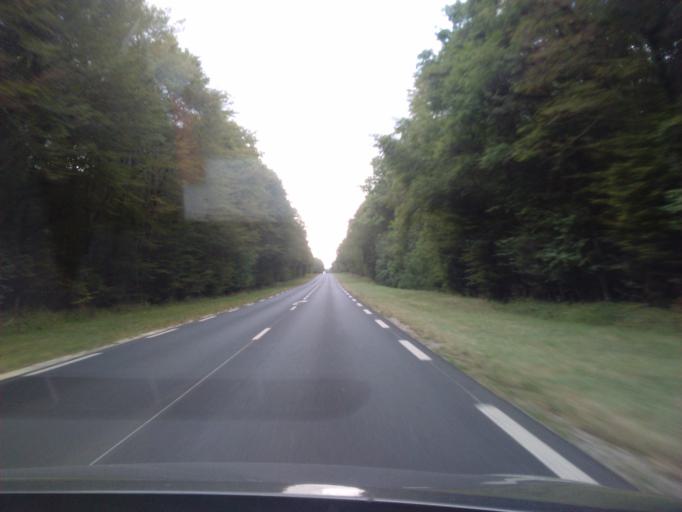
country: FR
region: Centre
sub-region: Departement du Loir-et-Cher
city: Cellettes
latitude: 47.5463
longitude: 1.3744
